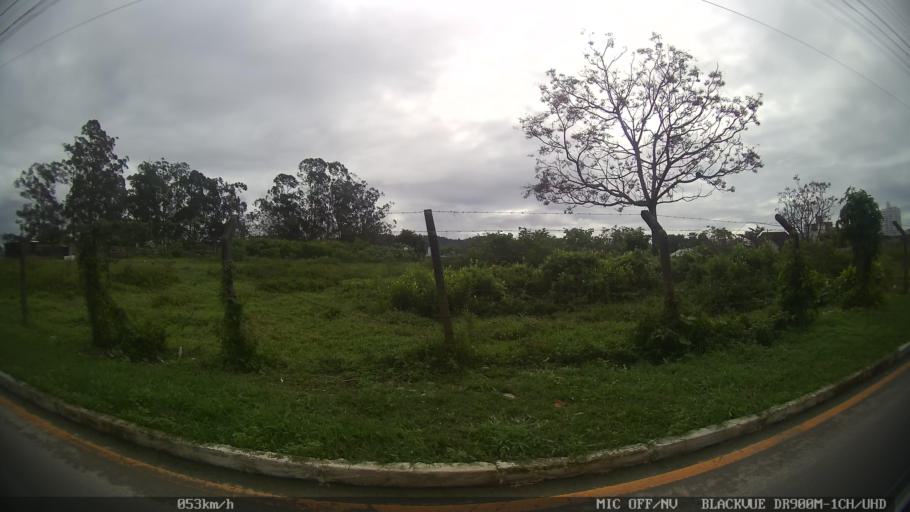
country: BR
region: Santa Catarina
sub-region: Sao Jose
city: Campinas
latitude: -27.5608
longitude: -48.6341
